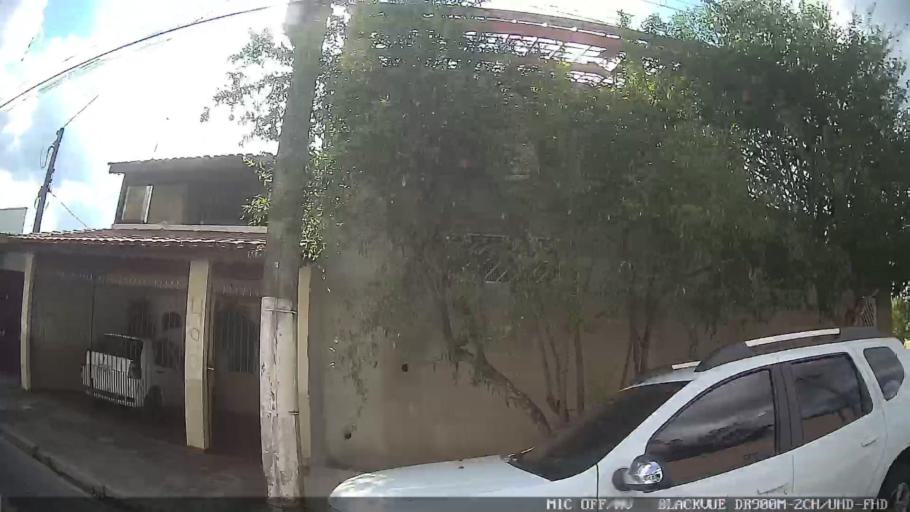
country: BR
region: Sao Paulo
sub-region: Atibaia
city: Atibaia
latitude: -23.1237
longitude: -46.5761
